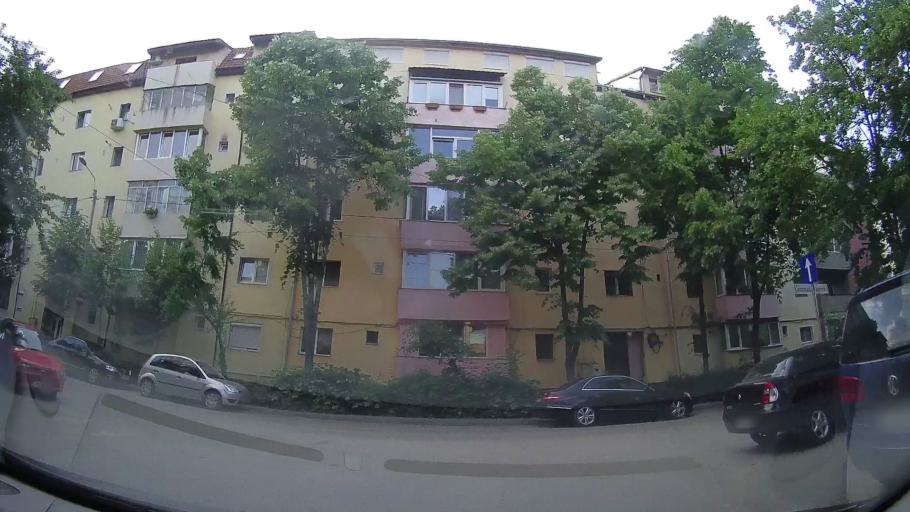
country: RO
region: Timis
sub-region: Comuna Dumbravita
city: Dumbravita
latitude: 45.7778
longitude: 21.2378
